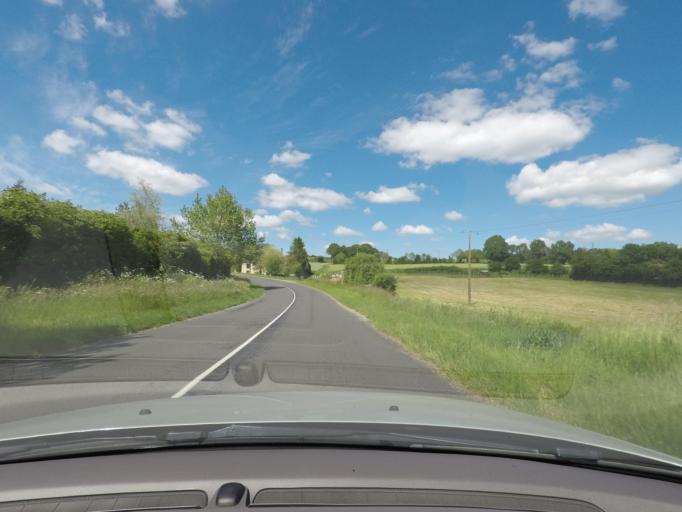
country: FR
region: Lower Normandy
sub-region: Departement de l'Orne
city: Mortagne-au-Perche
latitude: 48.5372
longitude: 0.5594
